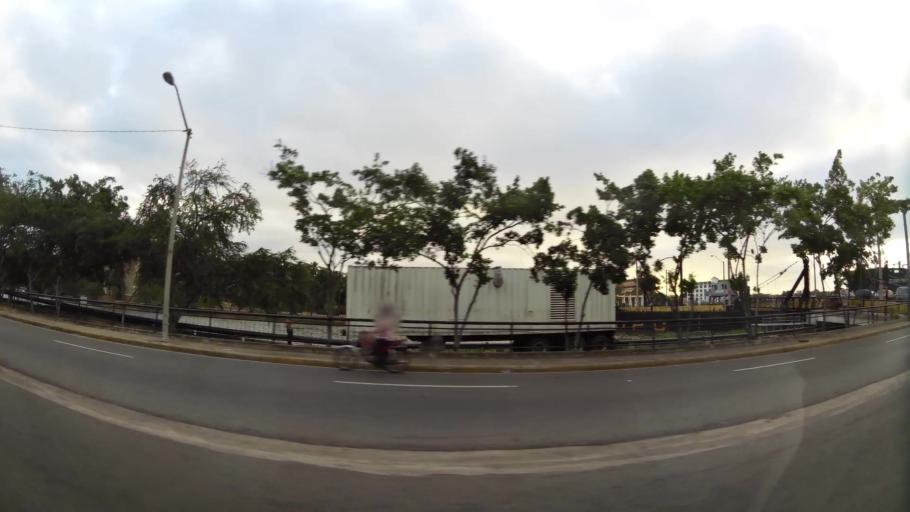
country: DO
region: Nacional
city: San Carlos
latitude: 18.4796
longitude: -69.8829
